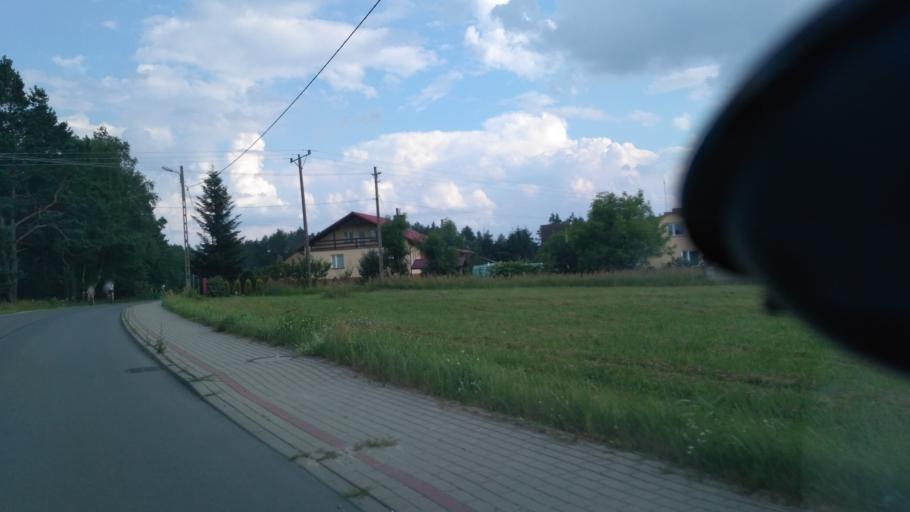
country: PL
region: Subcarpathian Voivodeship
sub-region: Powiat rzeszowski
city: Wysoka Glogowska
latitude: 50.1355
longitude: 22.0199
